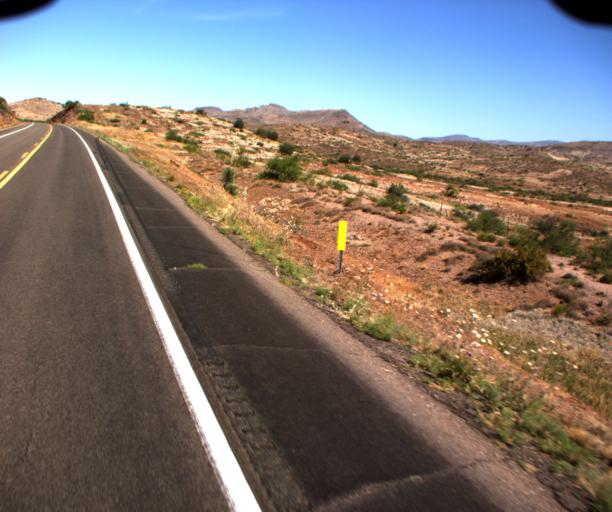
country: US
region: Arizona
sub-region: Greenlee County
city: Clifton
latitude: 32.7690
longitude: -109.2594
